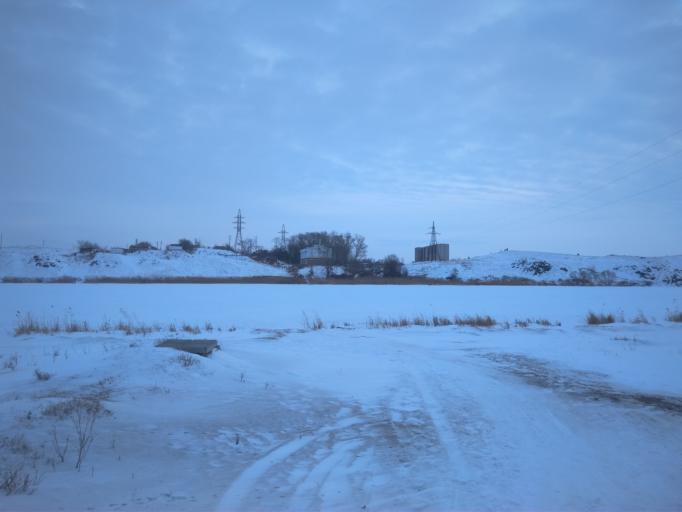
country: RU
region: Chelyabinsk
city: Troitsk
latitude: 54.0816
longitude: 61.5782
